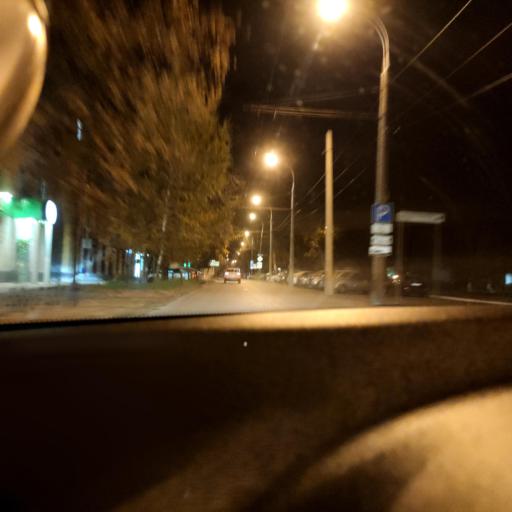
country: RU
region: Samara
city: Samara
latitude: 53.2172
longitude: 50.2515
